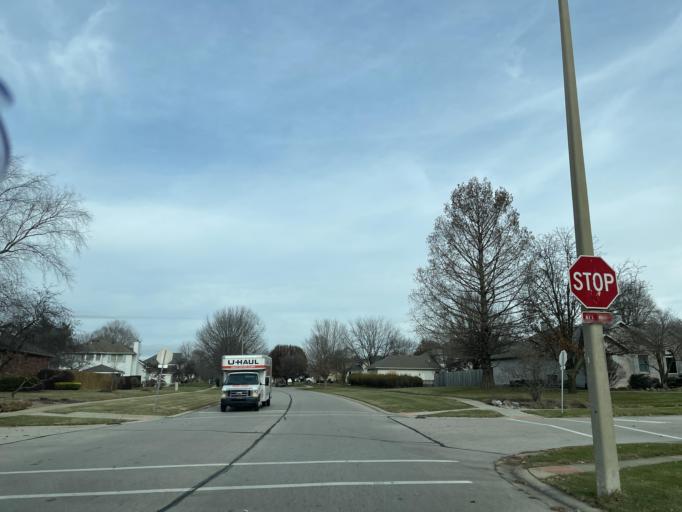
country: US
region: Illinois
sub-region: Sangamon County
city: Leland Grove
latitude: 39.7819
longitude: -89.7289
